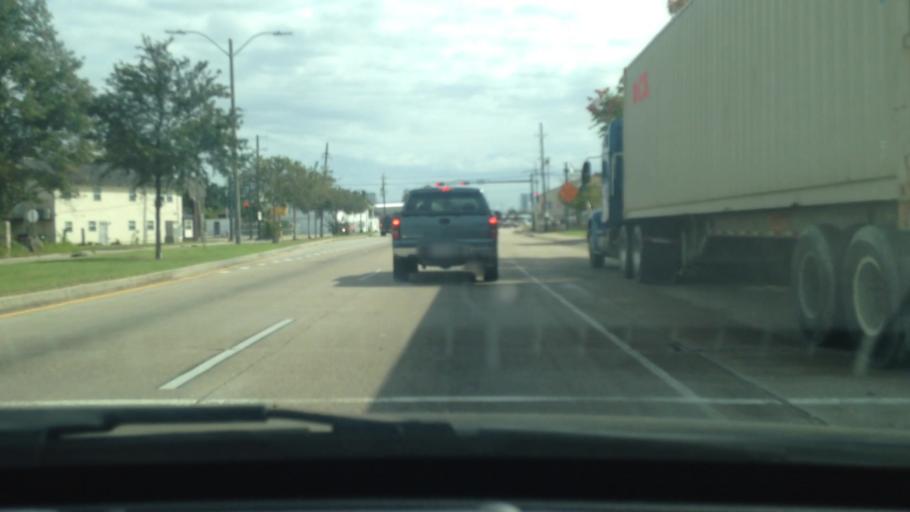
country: US
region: Louisiana
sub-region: Jefferson Parish
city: Jefferson
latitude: 29.9646
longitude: -90.1220
